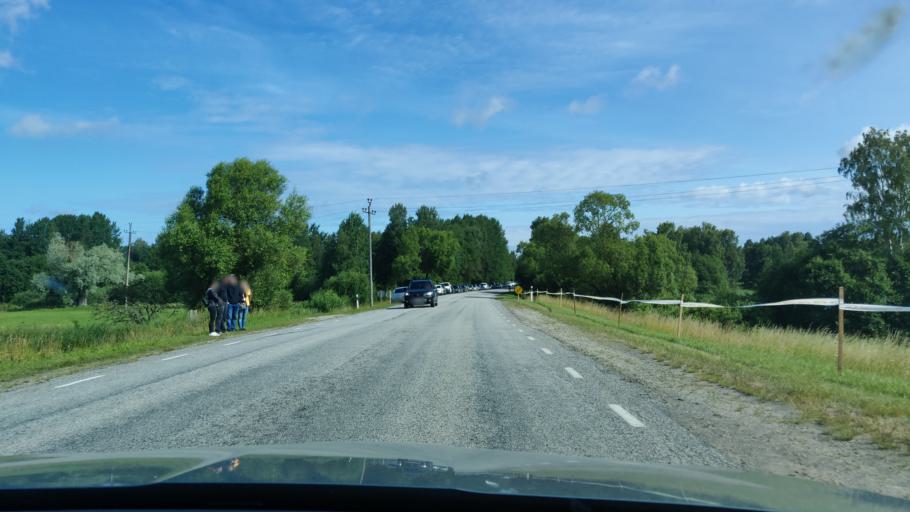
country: EE
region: Tartu
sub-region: Elva linn
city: Elva
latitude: 58.1382
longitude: 26.5208
